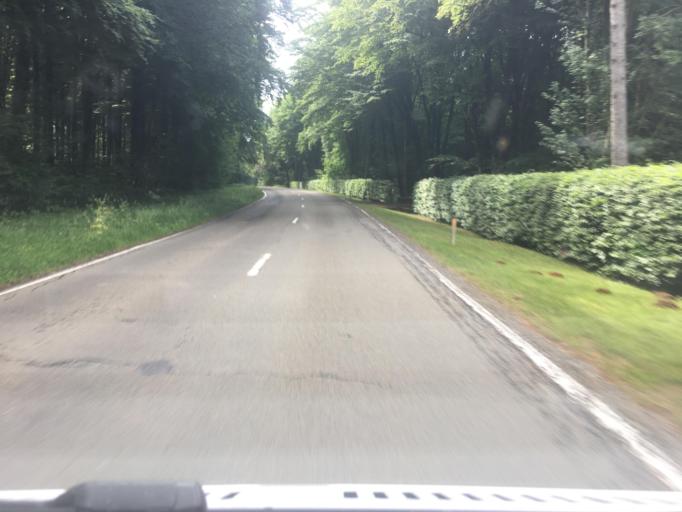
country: BE
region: Wallonia
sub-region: Province du Luxembourg
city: Florenville
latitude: 49.6483
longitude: 5.3392
